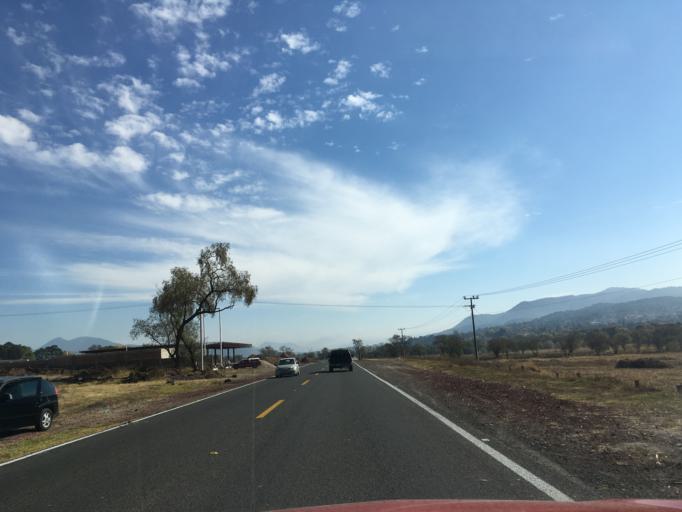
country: MX
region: Michoacan
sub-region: Hidalgo
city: San Lucas Huarirapeo (La Mesa de San Lucas)
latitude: 19.6805
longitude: -100.6446
